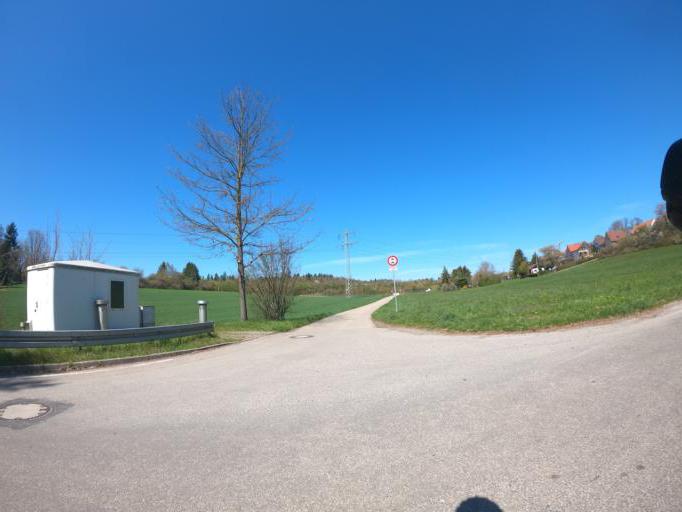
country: DE
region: Baden-Wuerttemberg
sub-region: Karlsruhe Region
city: Pforzheim
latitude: 48.9087
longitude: 8.7015
